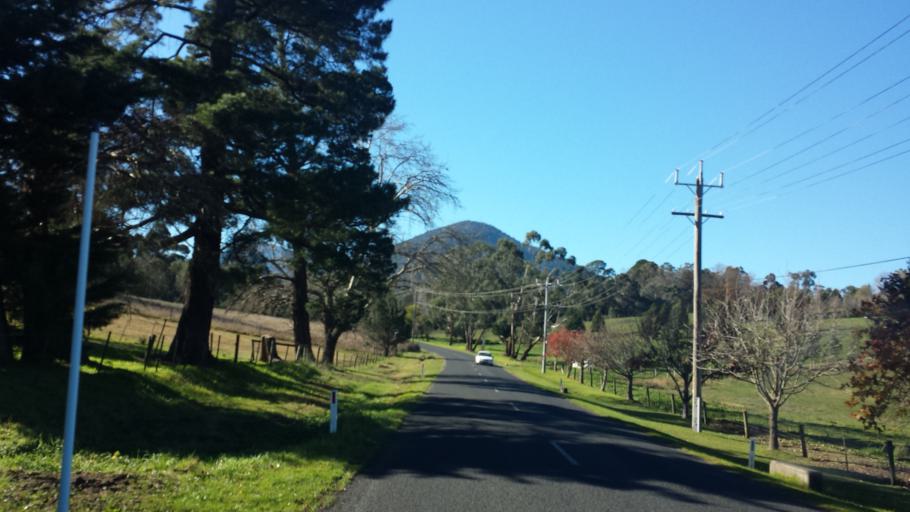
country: AU
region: Victoria
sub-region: Yarra Ranges
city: Healesville
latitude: -37.6711
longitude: 145.5199
